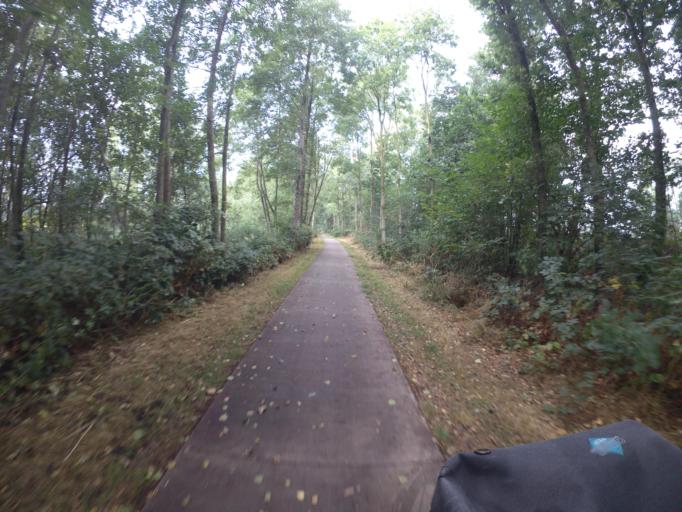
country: NL
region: Gelderland
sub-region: Gemeente Brummen
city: Eerbeek
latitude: 52.1601
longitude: 6.0608
